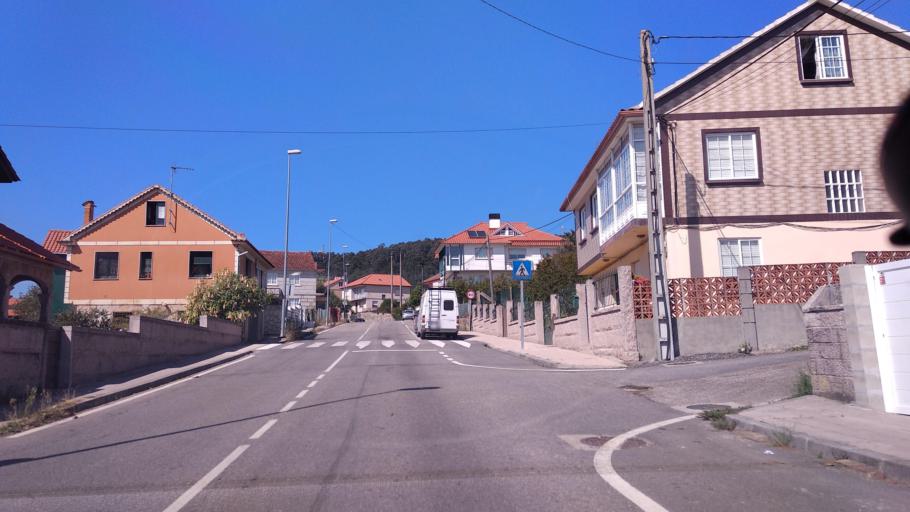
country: ES
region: Galicia
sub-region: Provincia de Pontevedra
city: Moana
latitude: 42.2742
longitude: -8.7675
